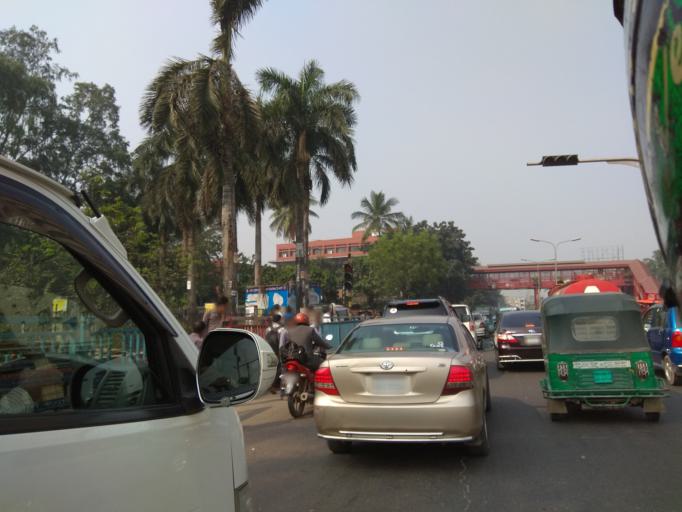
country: BD
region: Dhaka
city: Azimpur
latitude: 23.7588
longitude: 90.3898
